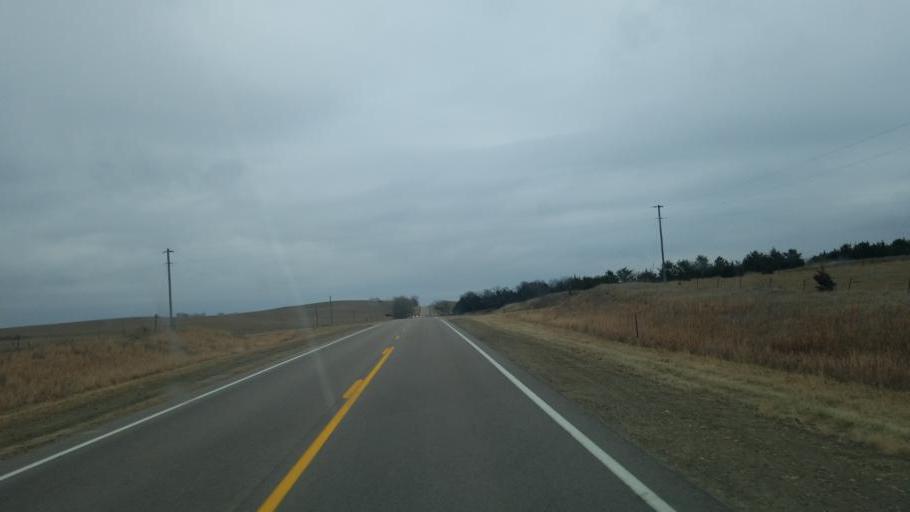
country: US
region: South Dakota
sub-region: Yankton County
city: Yankton
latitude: 42.7287
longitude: -97.4571
